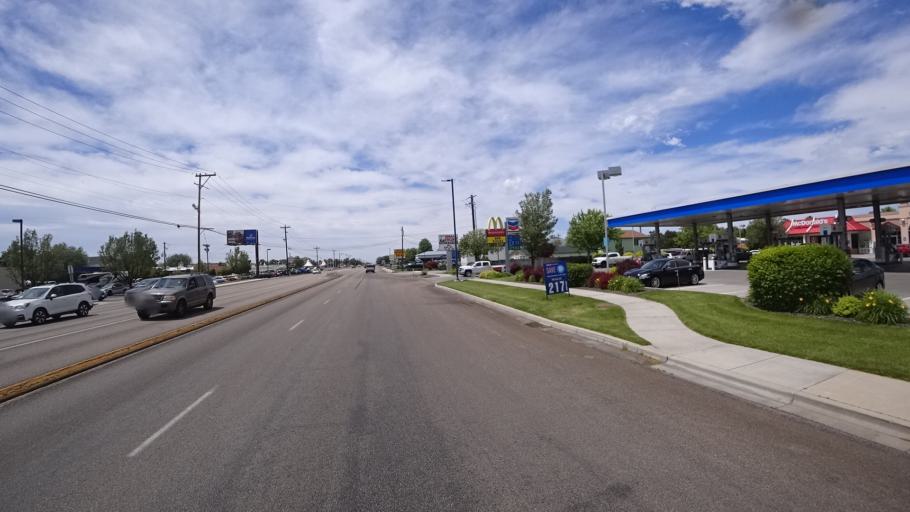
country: US
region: Idaho
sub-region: Ada County
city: Garden City
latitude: 43.6195
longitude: -116.3043
